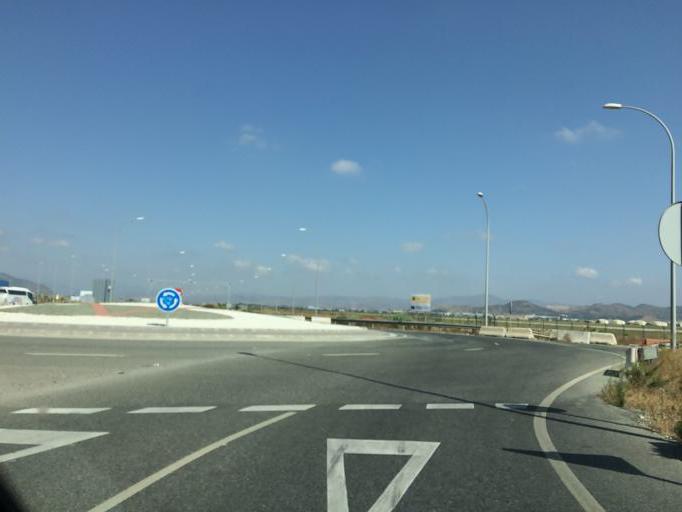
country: ES
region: Andalusia
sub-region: Provincia de Malaga
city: Torremolinos
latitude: 36.6834
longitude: -4.4979
